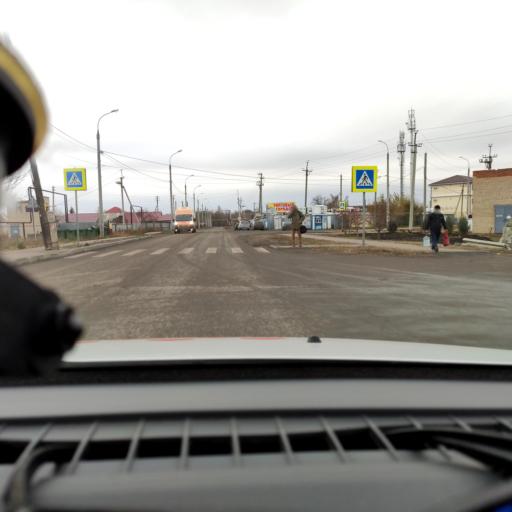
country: RU
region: Samara
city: Samara
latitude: 53.1339
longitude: 50.2357
